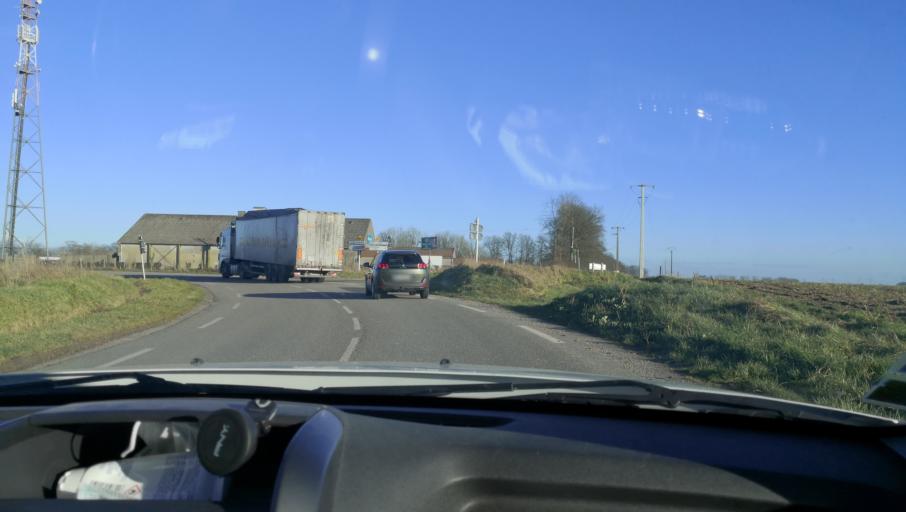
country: FR
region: Haute-Normandie
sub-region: Departement de la Seine-Maritime
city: Totes
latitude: 49.6745
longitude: 1.0489
